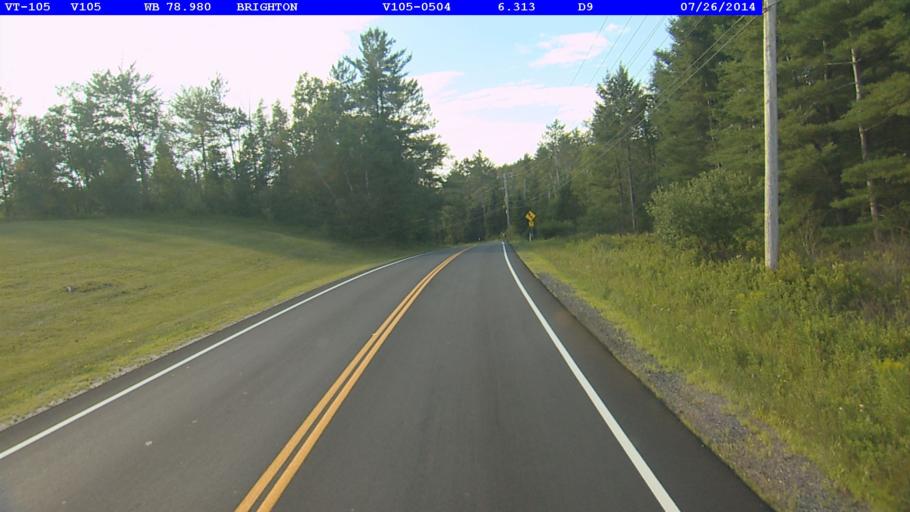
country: US
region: Vermont
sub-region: Caledonia County
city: Lyndonville
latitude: 44.8058
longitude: -71.8502
